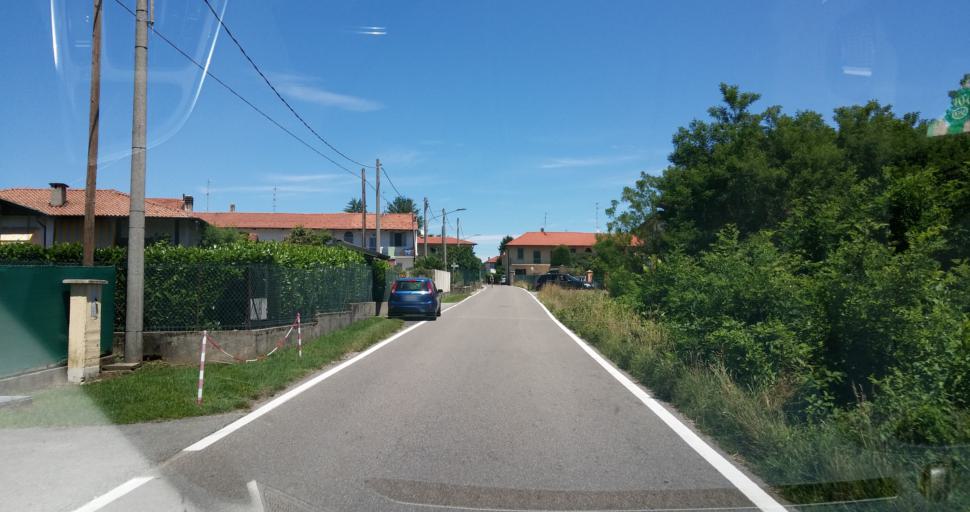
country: IT
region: Lombardy
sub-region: Provincia di Varese
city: Cimbro
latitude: 45.7456
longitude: 8.7248
